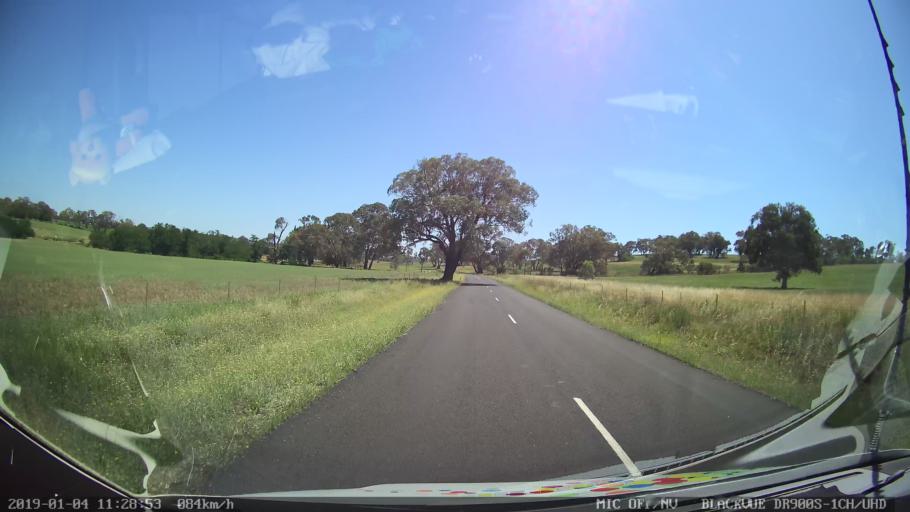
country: AU
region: New South Wales
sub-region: Cabonne
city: Molong
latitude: -33.0946
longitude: 148.7726
